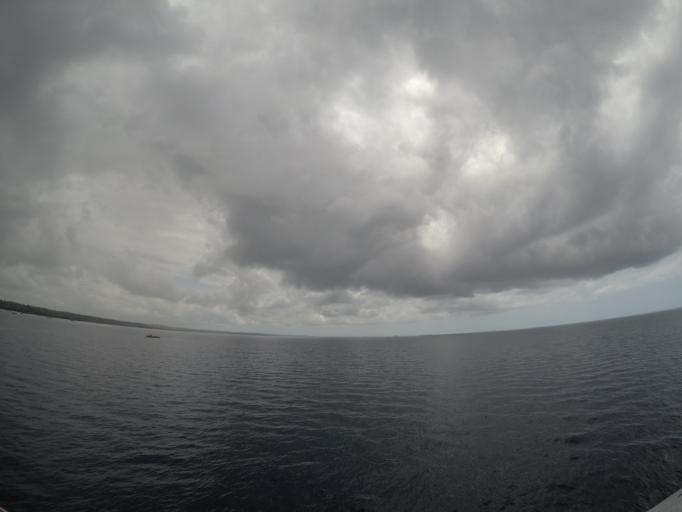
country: TZ
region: Zanzibar North
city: Mkokotoni
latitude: -5.9984
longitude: 39.1760
